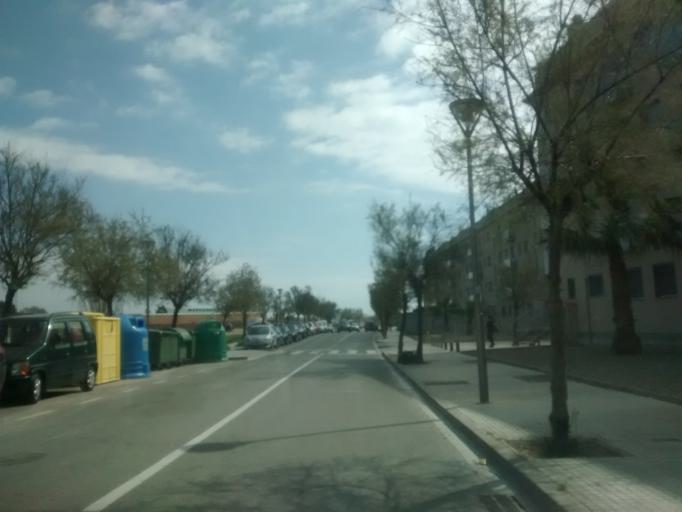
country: ES
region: Catalonia
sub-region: Provincia de Tarragona
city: Cunit
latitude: 41.1979
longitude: 1.6502
